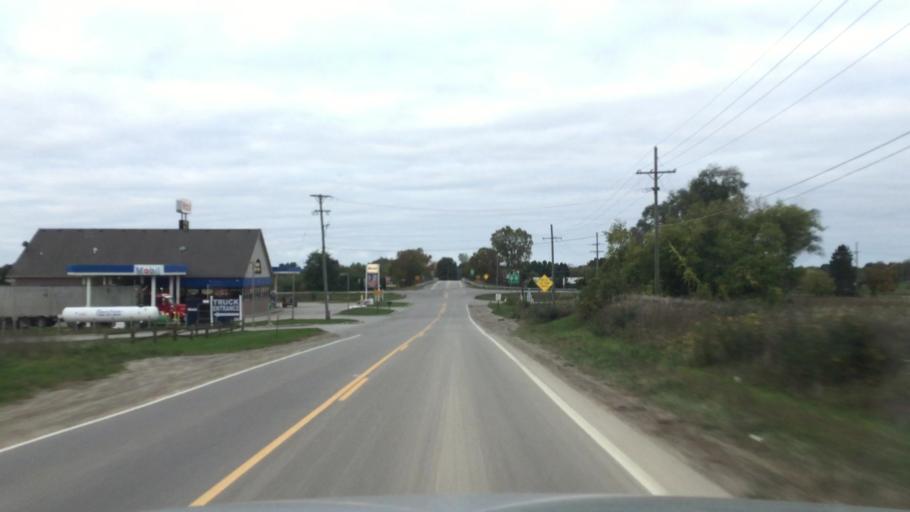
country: US
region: Michigan
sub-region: Genesee County
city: Fenton
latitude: 42.6769
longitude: -83.7561
